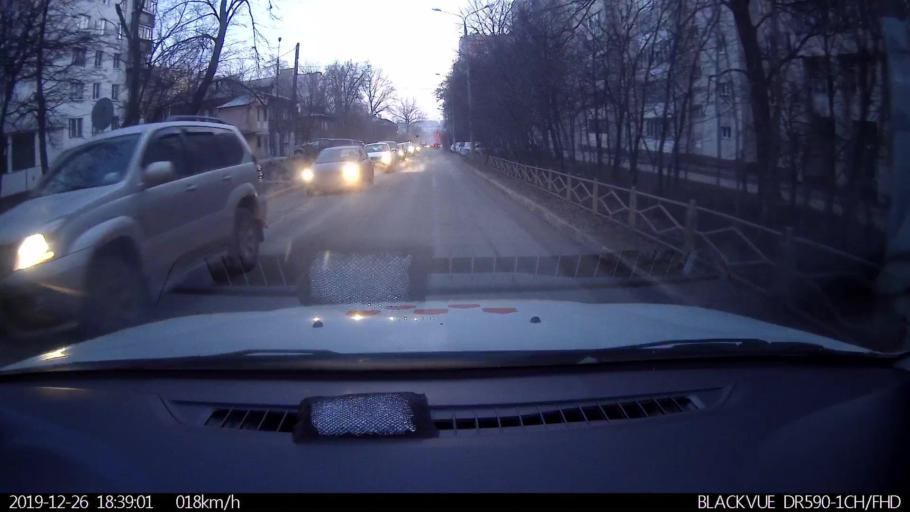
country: RU
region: Nizjnij Novgorod
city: Nizhniy Novgorod
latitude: 56.3117
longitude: 44.0249
